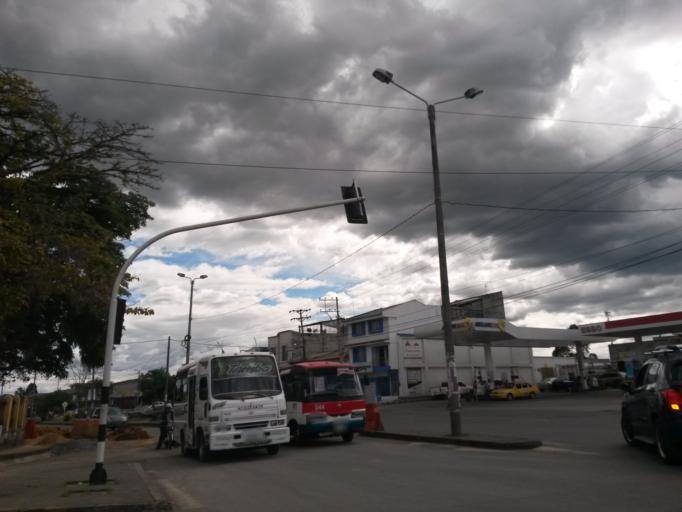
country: CO
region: Cauca
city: Popayan
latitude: 2.4564
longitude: -76.5914
